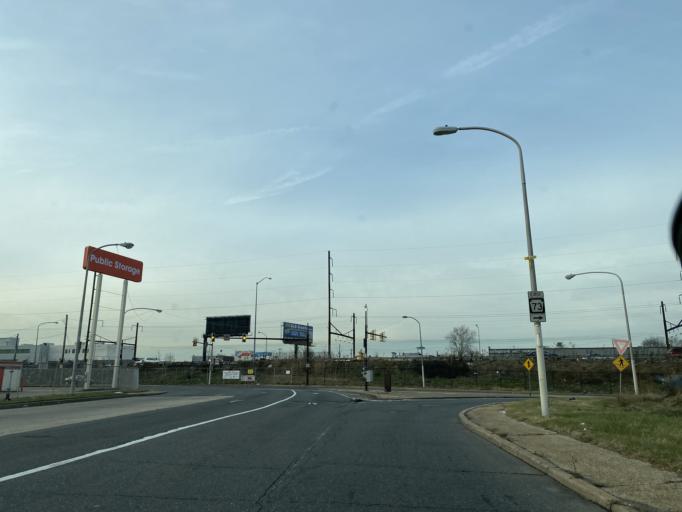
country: US
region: New Jersey
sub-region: Burlington County
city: Palmyra
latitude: 40.0166
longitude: -75.0489
